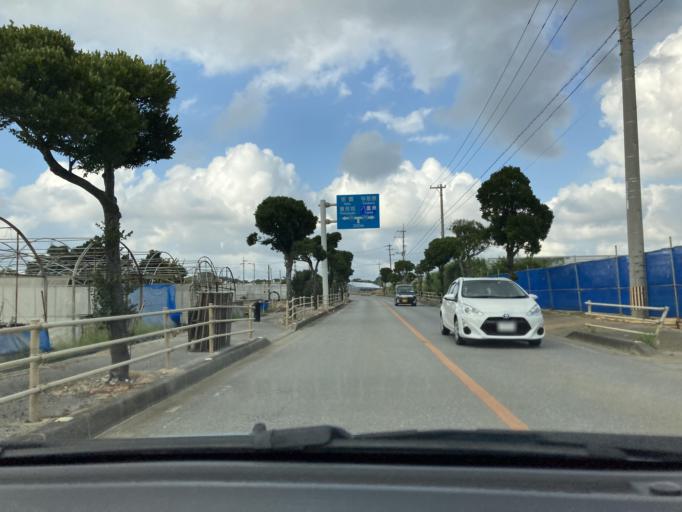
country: JP
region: Okinawa
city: Itoman
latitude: 26.1020
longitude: 127.6671
